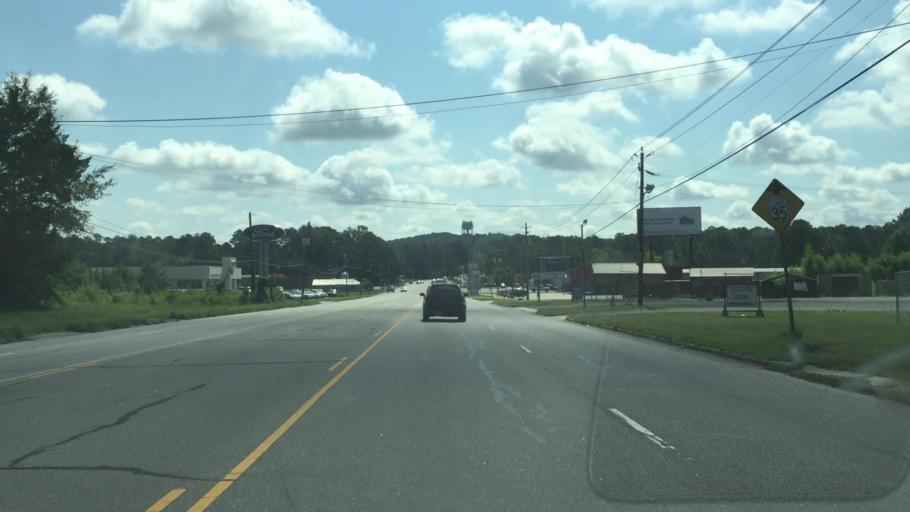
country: US
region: North Carolina
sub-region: Anson County
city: Wadesboro
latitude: 34.9787
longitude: -80.0967
